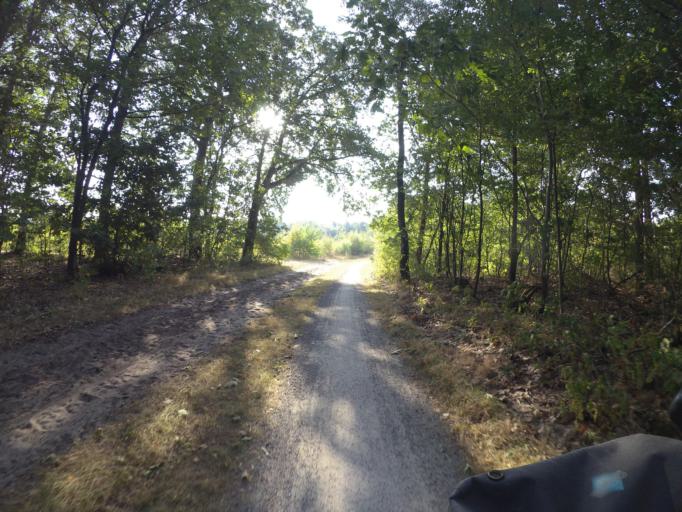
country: NL
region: Drenthe
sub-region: Gemeente Westerveld
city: Dwingeloo
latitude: 52.9227
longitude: 6.3267
